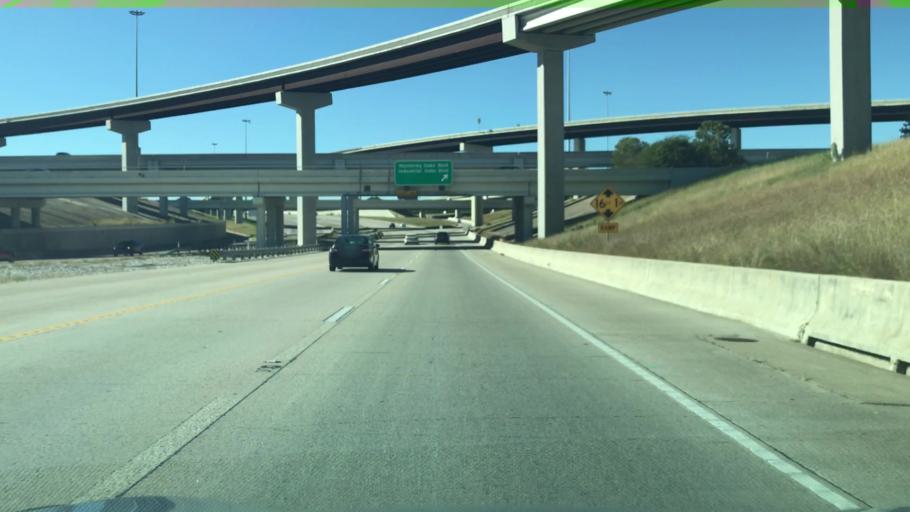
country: US
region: Texas
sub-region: Travis County
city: Rollingwood
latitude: 30.2347
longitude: -97.8227
